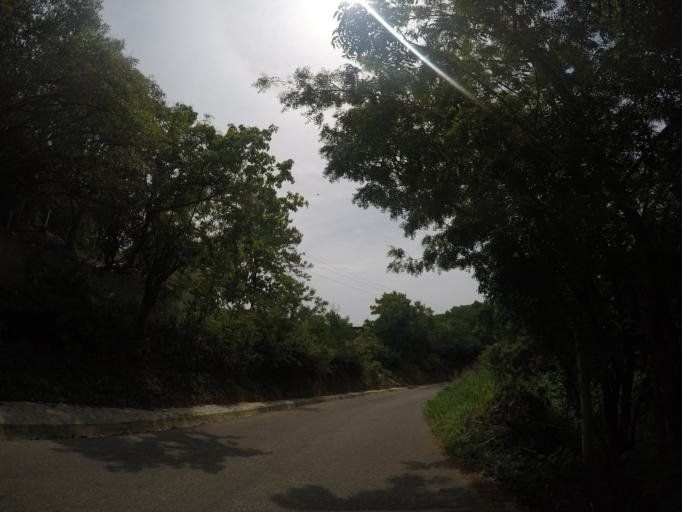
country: MX
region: Oaxaca
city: Santa Maria Tonameca
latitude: 15.6670
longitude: -96.5375
